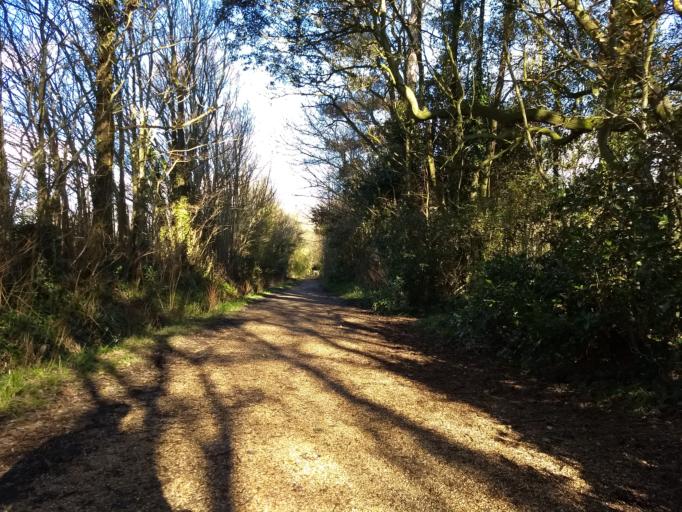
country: GB
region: England
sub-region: Isle of Wight
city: Ryde
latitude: 50.7310
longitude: -1.2090
